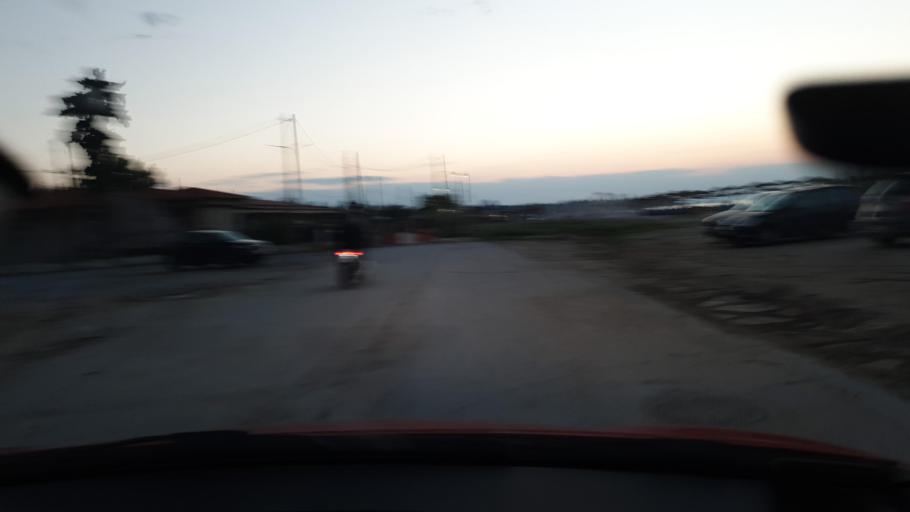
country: GR
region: Central Macedonia
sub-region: Nomos Thessalonikis
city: Neoi Epivates
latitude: 40.5023
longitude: 22.8936
